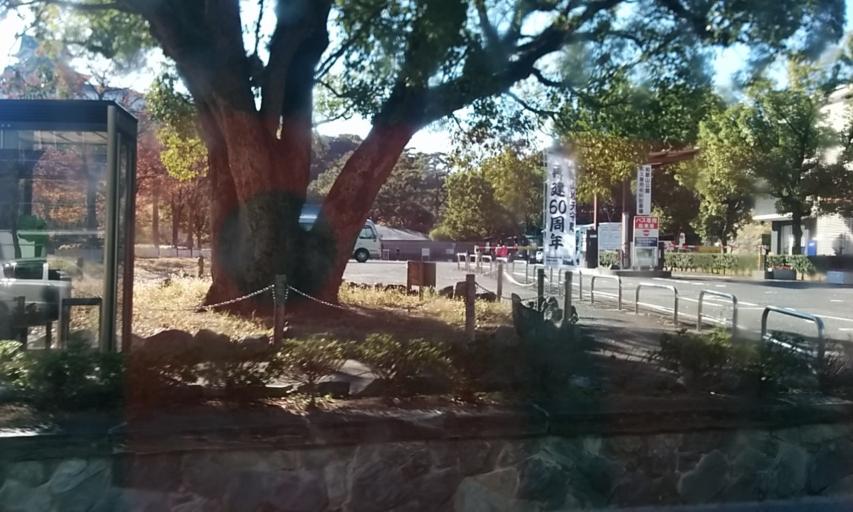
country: JP
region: Wakayama
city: Wakayama-shi
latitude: 34.2298
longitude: 135.1707
